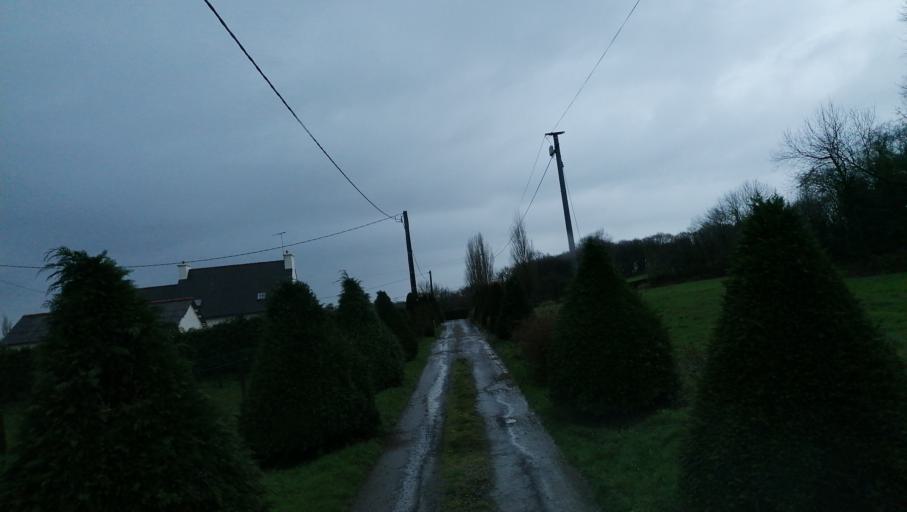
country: FR
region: Brittany
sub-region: Departement des Cotes-d'Armor
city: Plouagat
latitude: 48.4869
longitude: -2.9745
